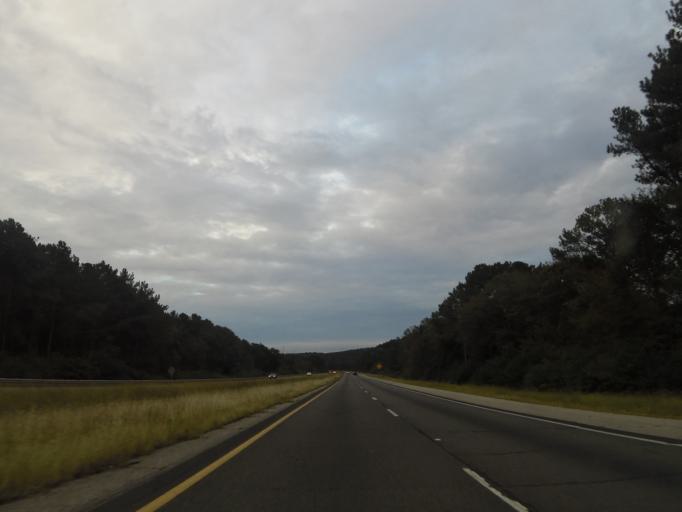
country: US
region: Alabama
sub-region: Jefferson County
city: Argo
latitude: 33.7228
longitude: -86.5084
